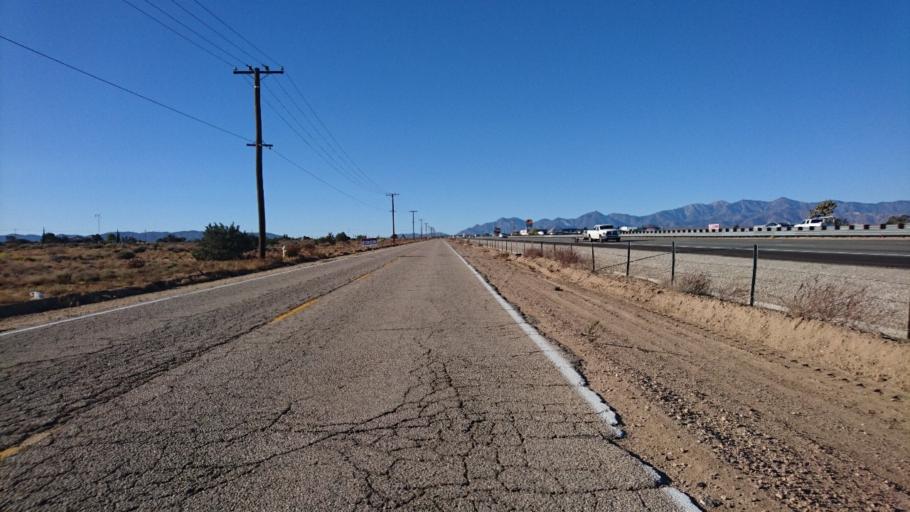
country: US
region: California
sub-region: San Bernardino County
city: Oak Hills
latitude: 34.4170
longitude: -117.3876
